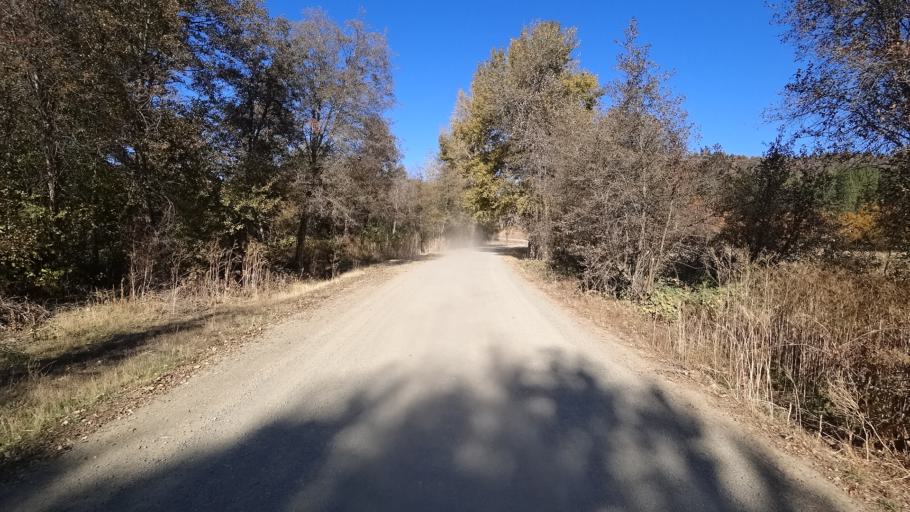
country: US
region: California
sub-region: Siskiyou County
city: Yreka
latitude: 41.6038
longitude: -122.9598
